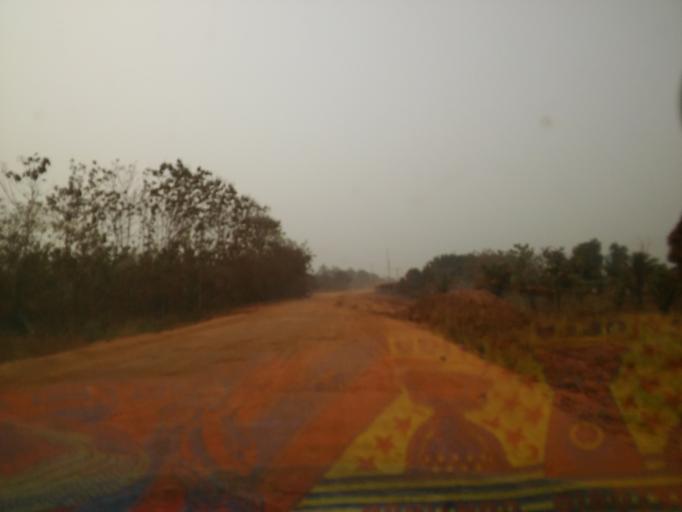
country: BJ
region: Kouffo
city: Dogbo
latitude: 6.7384
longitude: 1.7679
